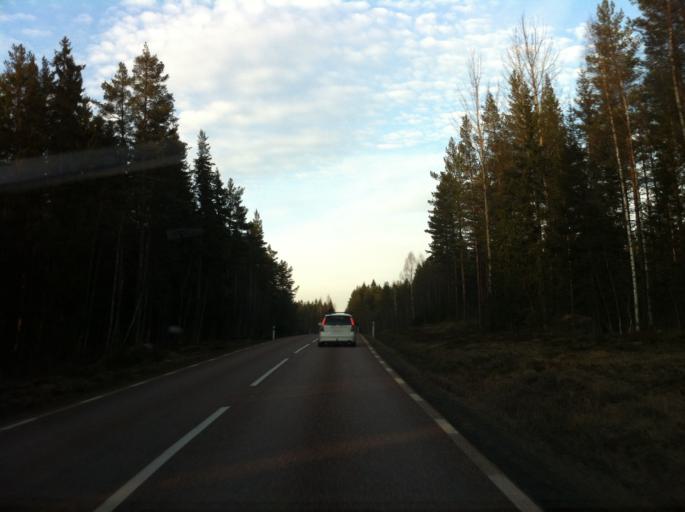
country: SE
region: Dalarna
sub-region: Vansbro Kommun
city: Vansbro
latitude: 60.4910
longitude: 14.2385
